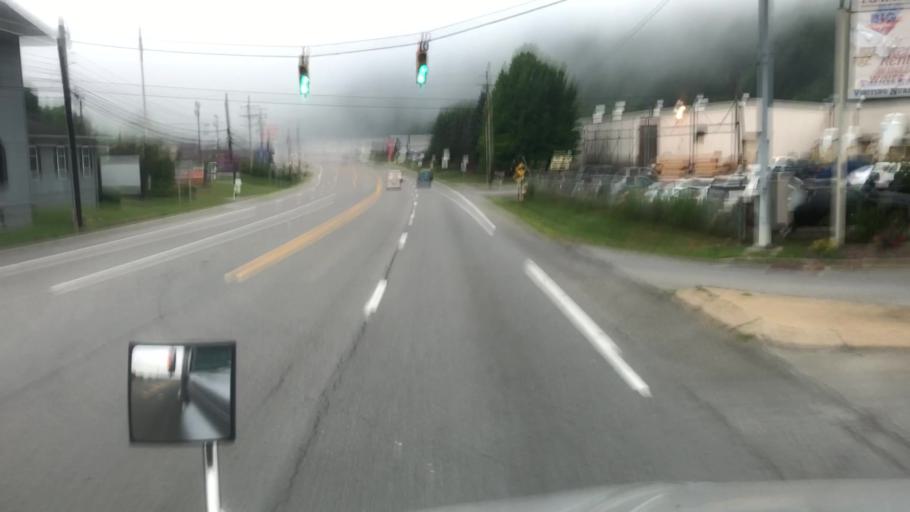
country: US
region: Pennsylvania
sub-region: Venango County
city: Franklin
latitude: 41.4016
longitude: -79.8107
